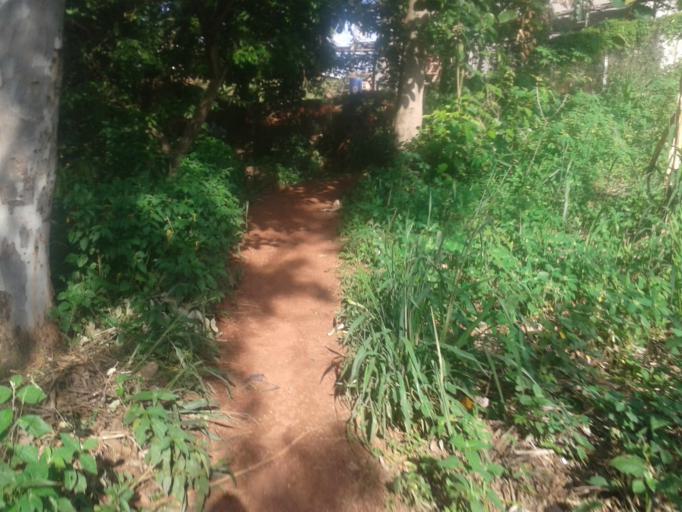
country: UG
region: Northern Region
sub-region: Gulu District
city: Gulu
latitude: 2.7886
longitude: 32.3155
